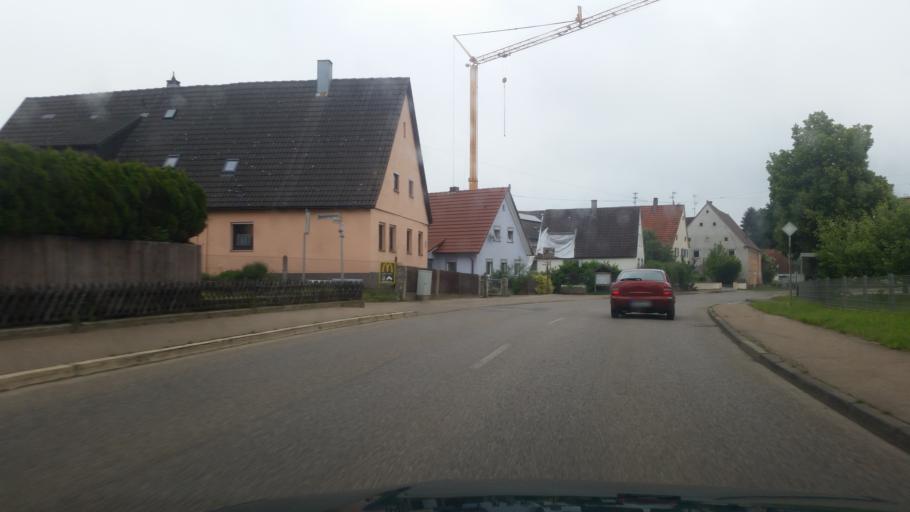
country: DE
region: Baden-Wuerttemberg
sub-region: Regierungsbezirk Stuttgart
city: Kirchheim am Ries
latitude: 48.8443
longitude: 10.3917
